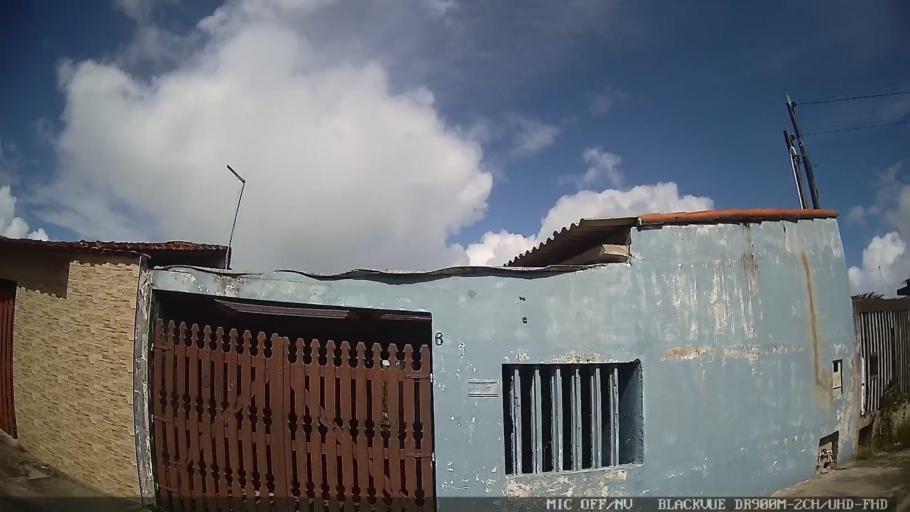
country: BR
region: Sao Paulo
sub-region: Itanhaem
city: Itanhaem
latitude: -24.2422
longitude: -46.8946
